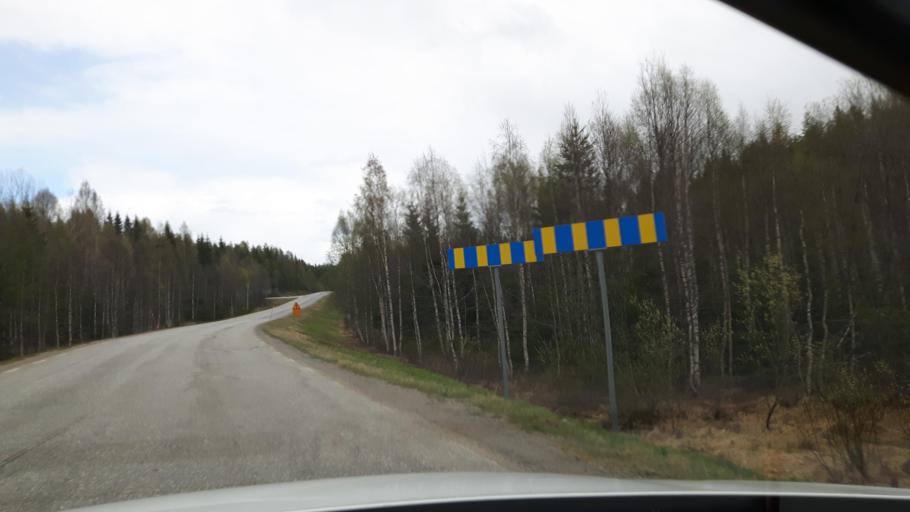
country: SE
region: Vaesterbotten
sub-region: Skelleftea Kommun
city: Burtraesk
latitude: 64.2688
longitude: 20.5452
